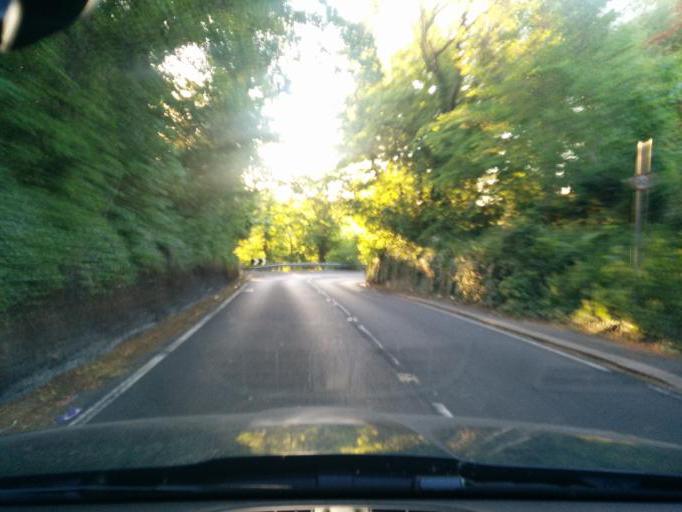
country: GB
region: England
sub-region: Northumberland
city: Bedlington
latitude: 55.1241
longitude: -1.5814
